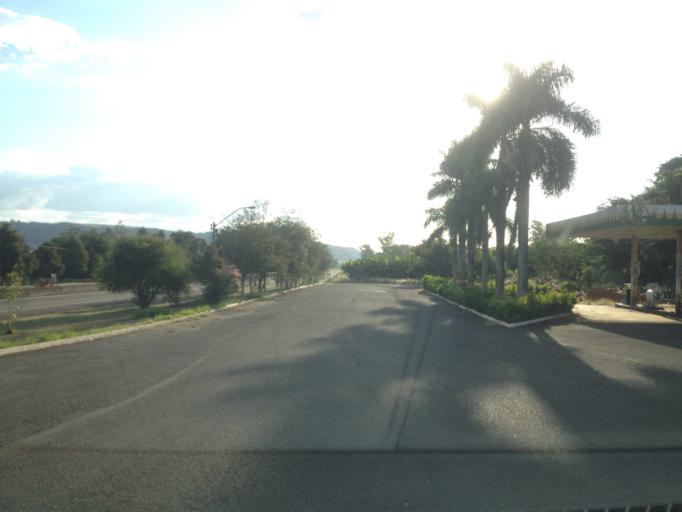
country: BR
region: Sao Paulo
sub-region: Brotas
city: Brotas
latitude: -22.2655
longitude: -48.2141
